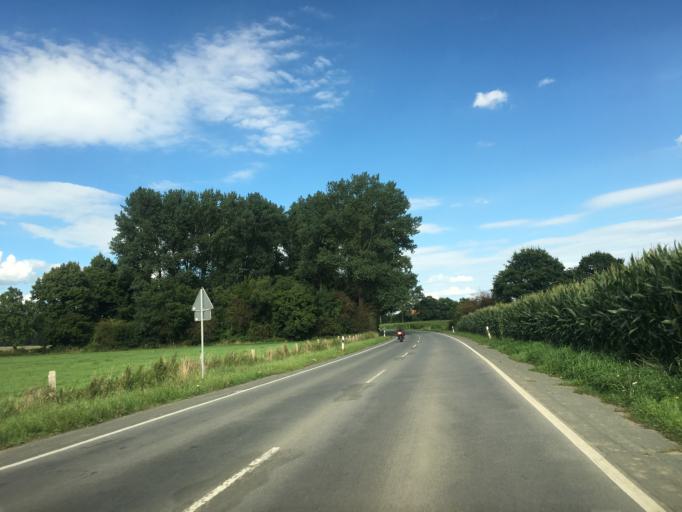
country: DE
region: North Rhine-Westphalia
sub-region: Regierungsbezirk Munster
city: Nordkirchen
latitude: 51.7238
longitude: 7.5006
